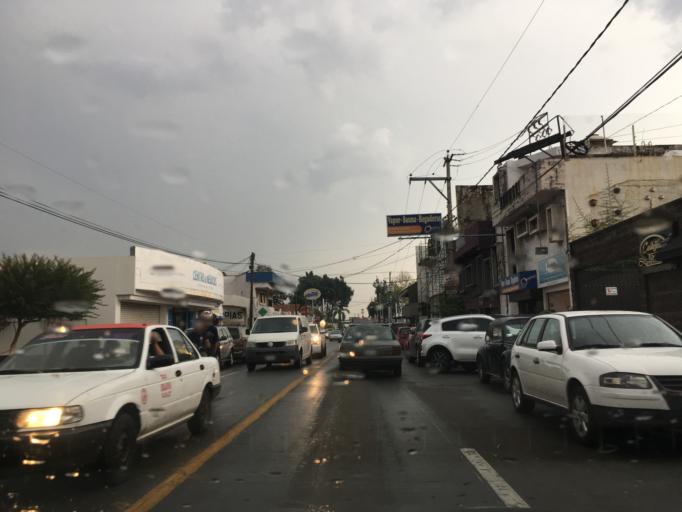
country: MX
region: Michoacan
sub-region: Uruapan
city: Uruapan
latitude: 19.4135
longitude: -102.0541
